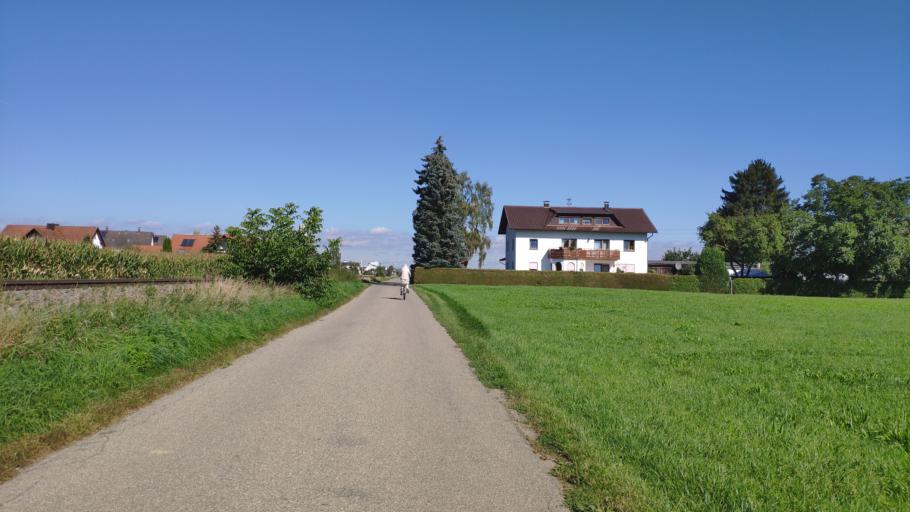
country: DE
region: Bavaria
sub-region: Swabia
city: Senden
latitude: 48.3400
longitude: 10.0405
